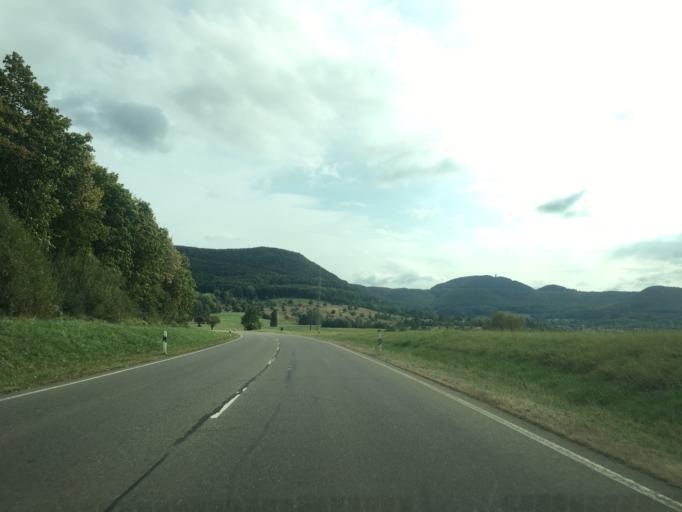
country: DE
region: Baden-Wuerttemberg
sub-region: Tuebingen Region
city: Gomaringen
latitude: 48.4539
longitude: 9.1510
